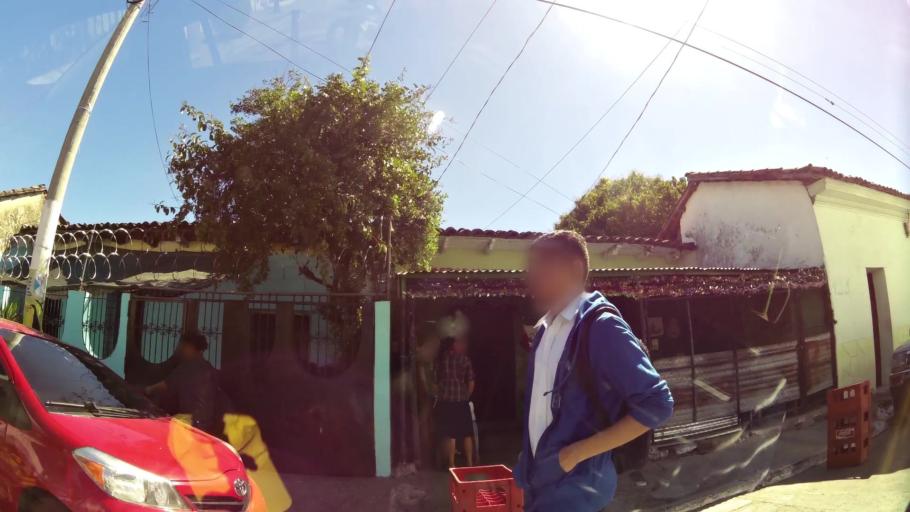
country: SV
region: La Libertad
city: San Juan Opico
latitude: 13.8763
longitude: -89.3576
